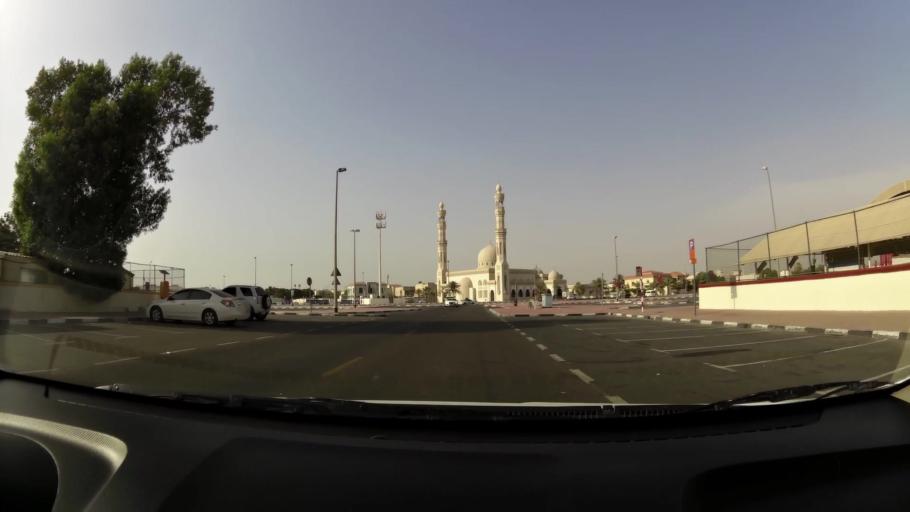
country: AE
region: Ash Shariqah
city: Sharjah
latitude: 25.2366
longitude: 55.3504
